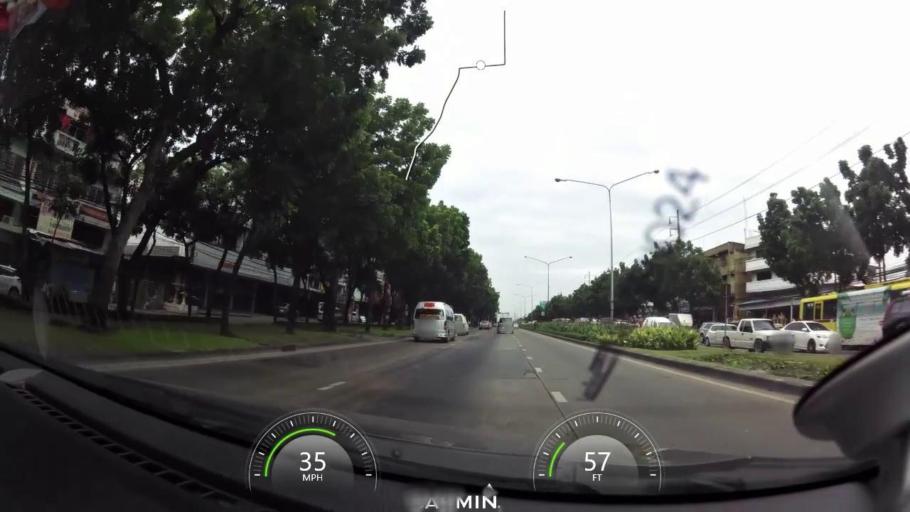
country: TH
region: Bangkok
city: Nong Khaem
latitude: 13.7058
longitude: 100.3473
